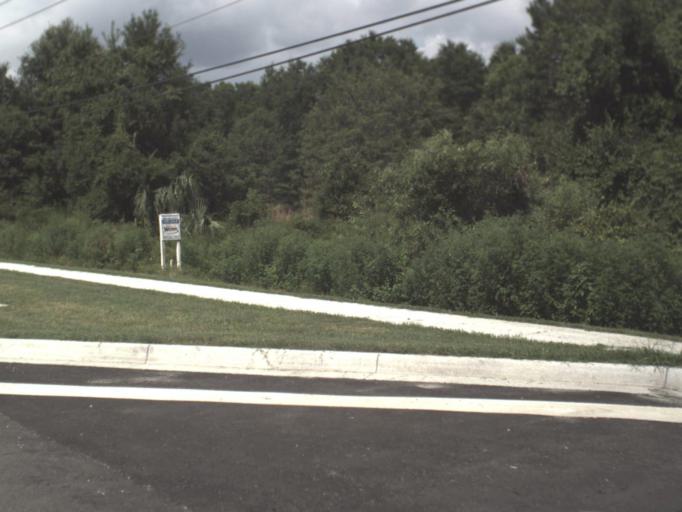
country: US
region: Florida
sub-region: Saint Johns County
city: Fruit Cove
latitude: 30.0902
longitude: -81.6294
